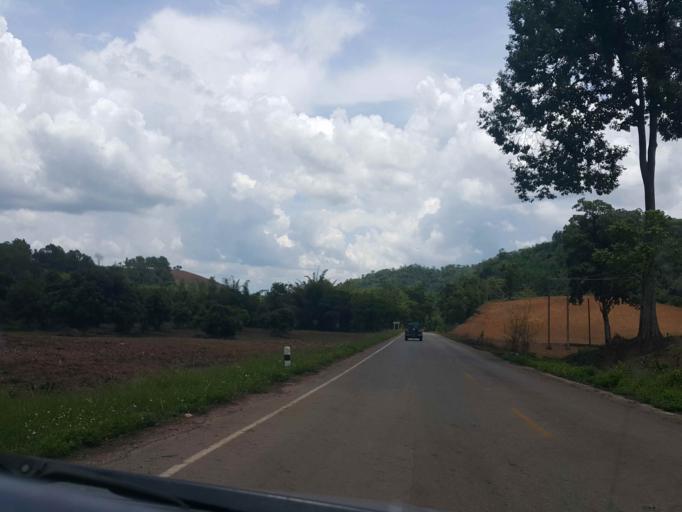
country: TH
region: Phayao
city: Chiang Muan
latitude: 18.8993
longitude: 100.1335
